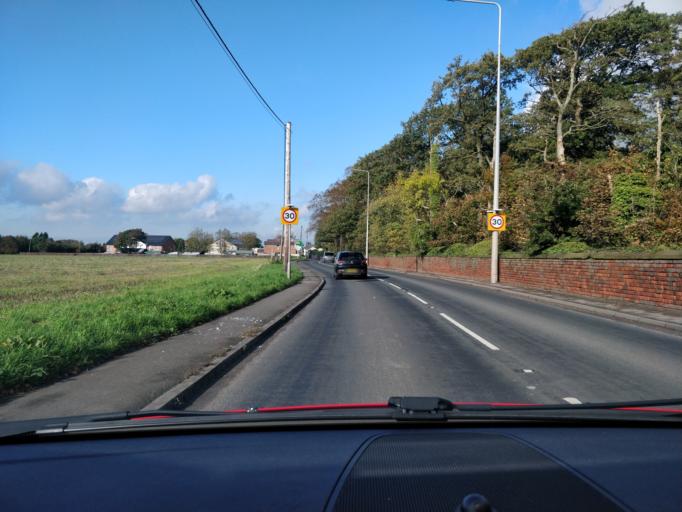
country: GB
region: England
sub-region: Lancashire
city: Ormskirk
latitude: 53.6078
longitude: -2.9334
